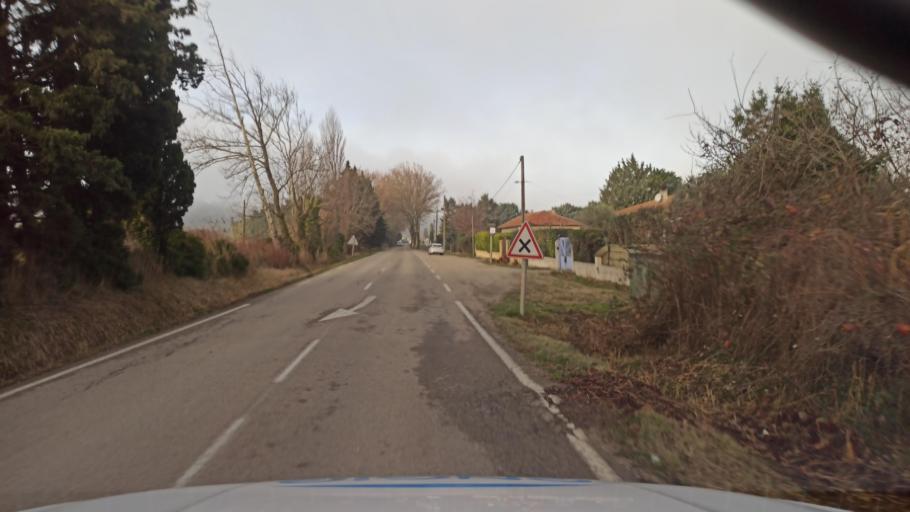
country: FR
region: Provence-Alpes-Cote d'Azur
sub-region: Departement des Bouches-du-Rhone
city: Rognonas
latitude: 43.8971
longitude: 4.7771
